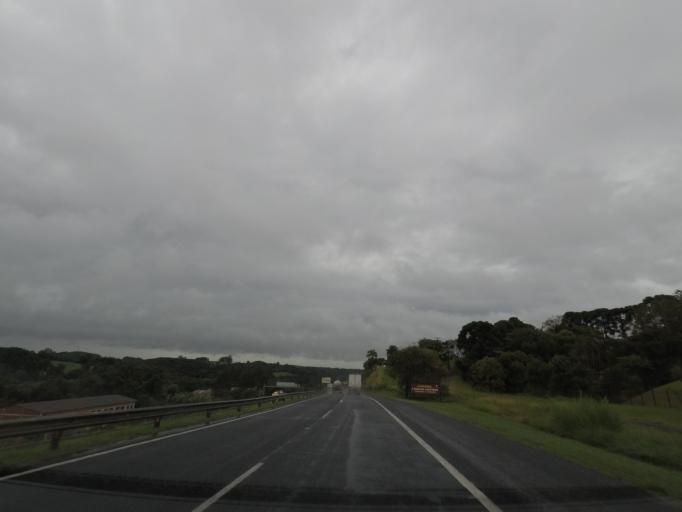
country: BR
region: Parana
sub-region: Curitiba
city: Curitiba
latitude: -25.4322
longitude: -49.4009
